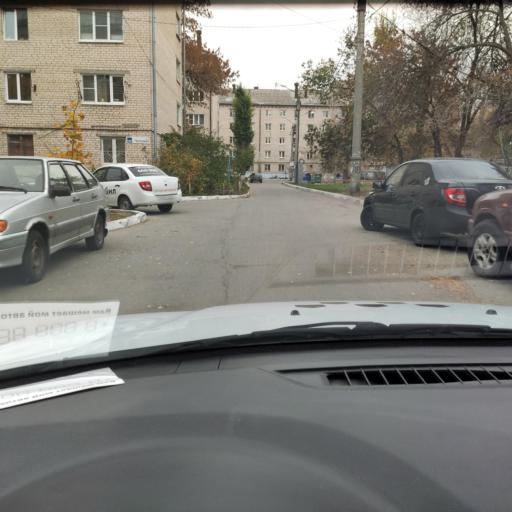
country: RU
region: Samara
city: Tol'yatti
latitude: 53.5227
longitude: 49.4251
